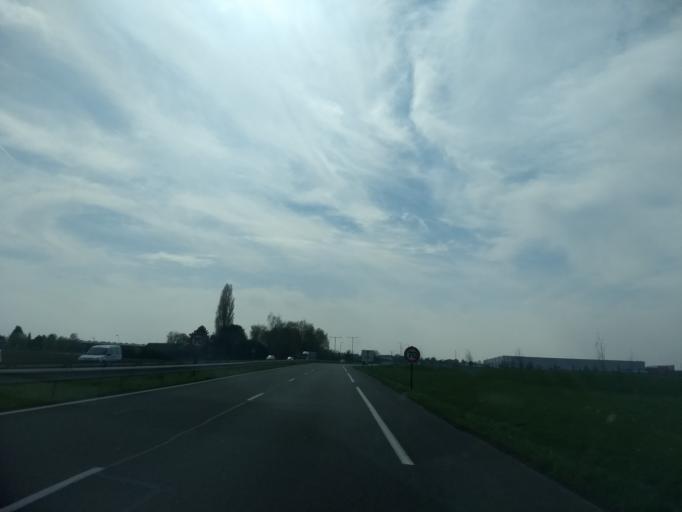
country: FR
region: Nord-Pas-de-Calais
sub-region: Departement du Pas-de-Calais
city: Corbehem
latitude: 50.3493
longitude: 3.0363
